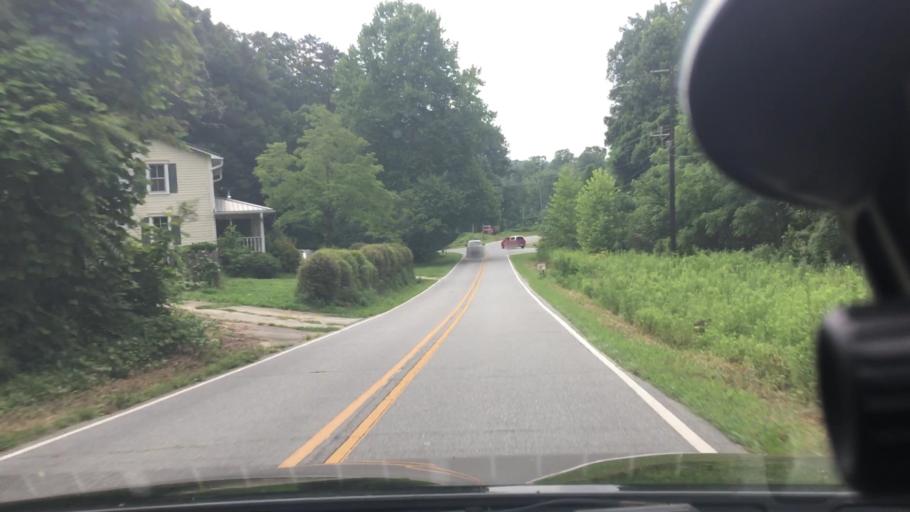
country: US
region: North Carolina
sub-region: McDowell County
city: West Marion
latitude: 35.6553
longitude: -82.0159
